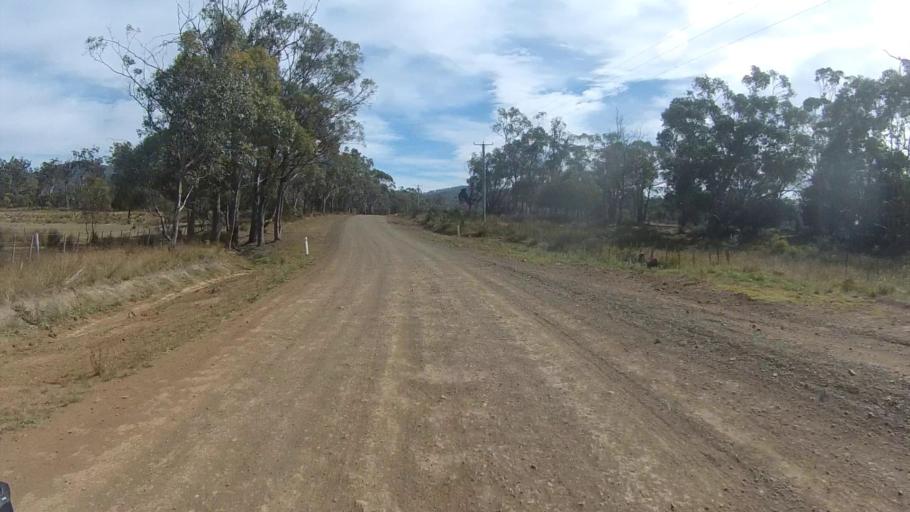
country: AU
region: Tasmania
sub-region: Sorell
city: Sorell
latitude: -42.6486
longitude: 147.8993
